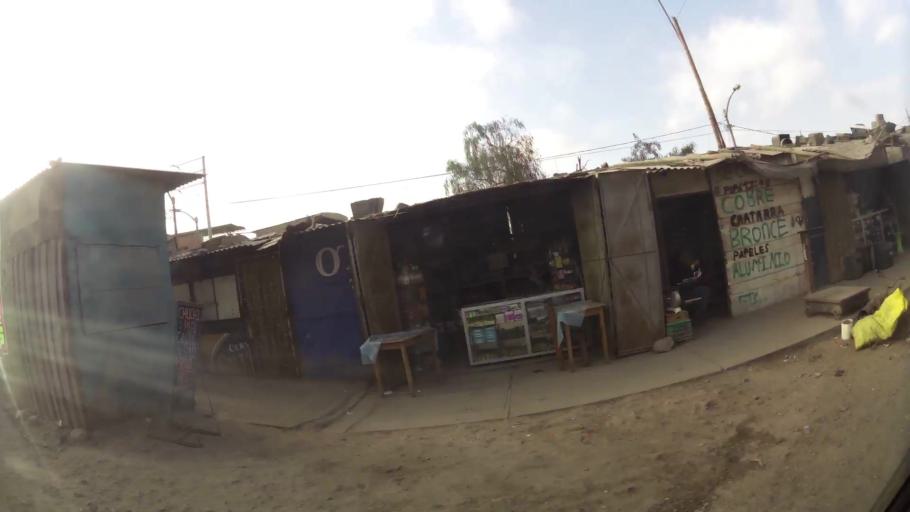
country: PE
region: La Libertad
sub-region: Provincia de Trujillo
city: La Esperanza
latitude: -8.0891
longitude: -79.0263
